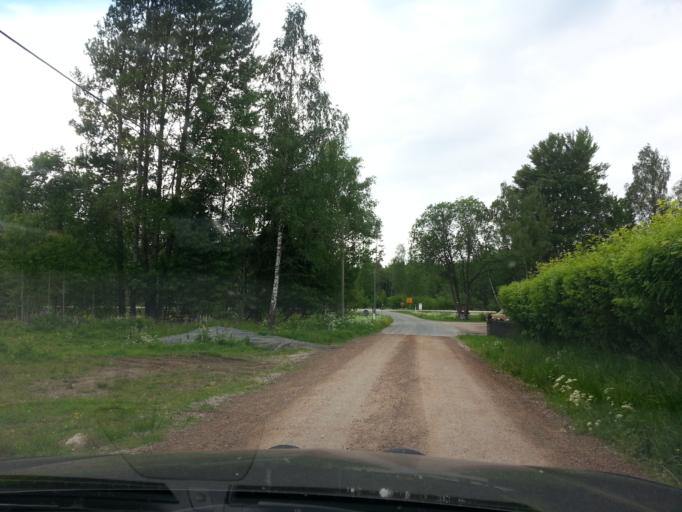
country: SE
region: Joenkoeping
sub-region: Vetlanda Kommun
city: Vetlanda
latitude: 57.2855
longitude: 15.1334
